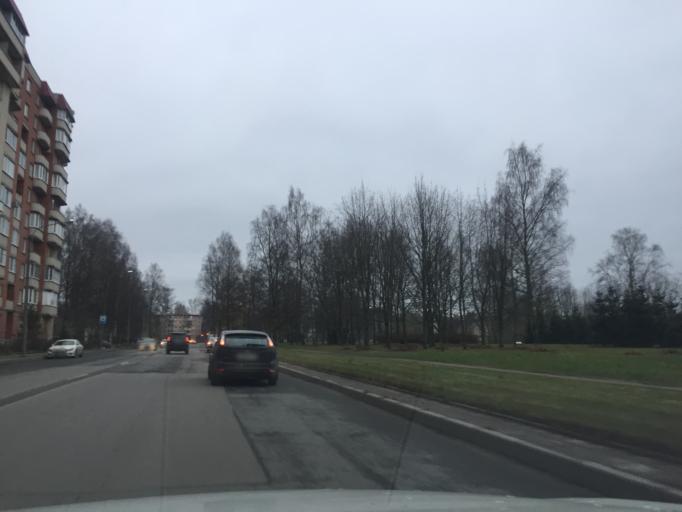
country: RU
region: Leningrad
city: Akademicheskoe
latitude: 60.0203
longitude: 30.3737
